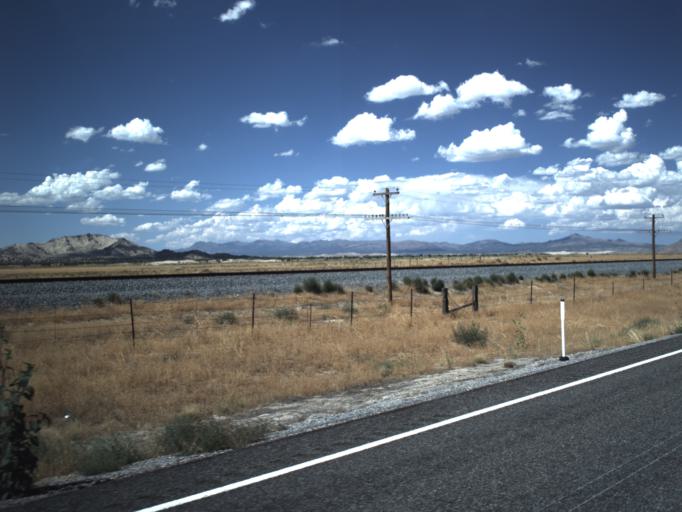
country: US
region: Utah
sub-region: Millard County
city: Delta
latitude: 39.5594
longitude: -112.3507
